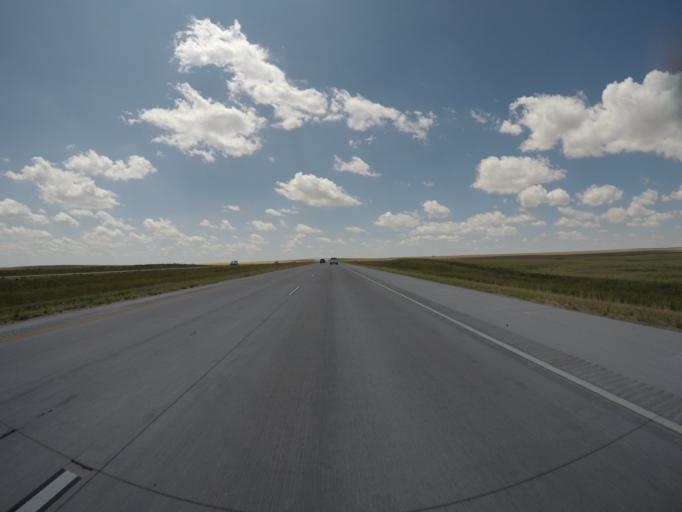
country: US
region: Colorado
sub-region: Kit Carson County
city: Burlington
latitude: 39.2942
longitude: -102.7695
